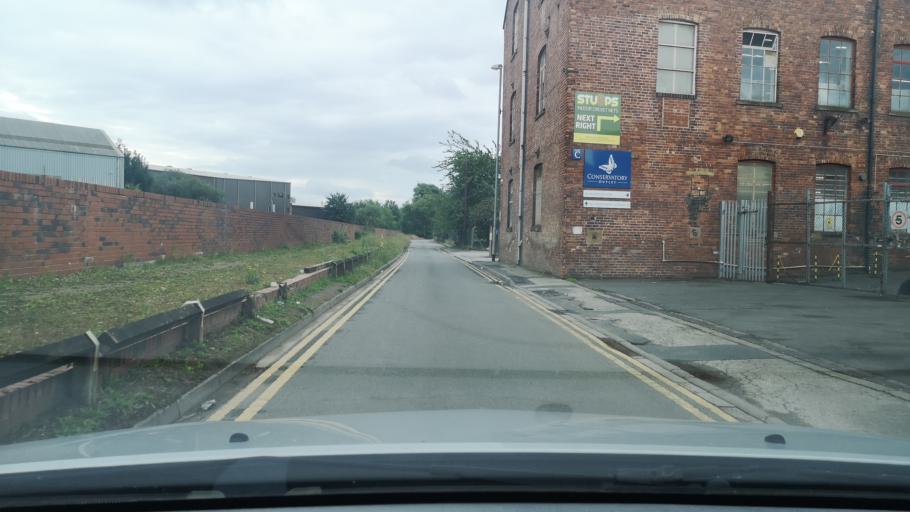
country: GB
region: England
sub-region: City and Borough of Wakefield
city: Wakefield
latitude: 53.6718
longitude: -1.4922
